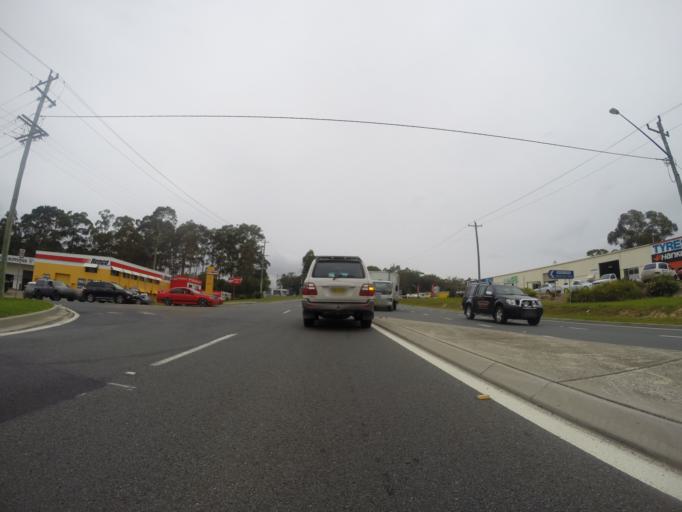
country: AU
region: New South Wales
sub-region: Eurobodalla
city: Batemans Bay
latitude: -35.7194
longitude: 150.1760
